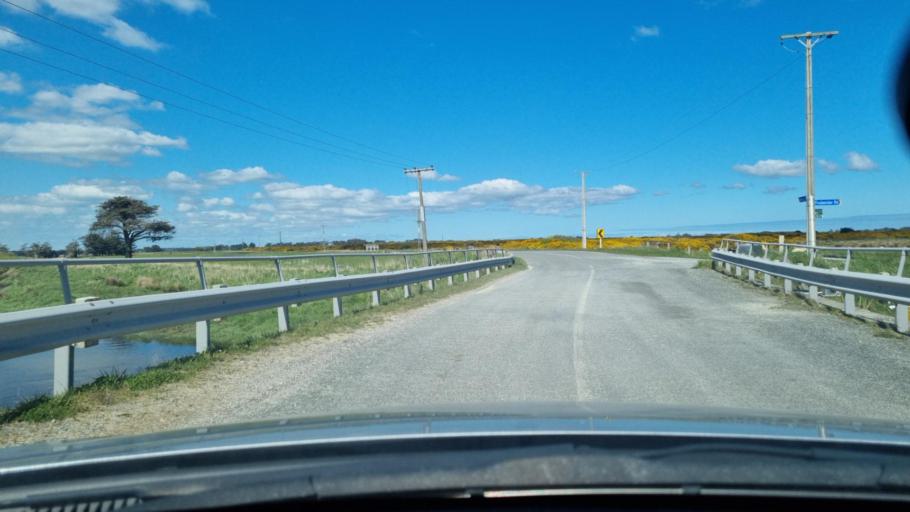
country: NZ
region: Southland
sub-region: Invercargill City
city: Invercargill
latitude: -46.3906
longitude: 168.2618
